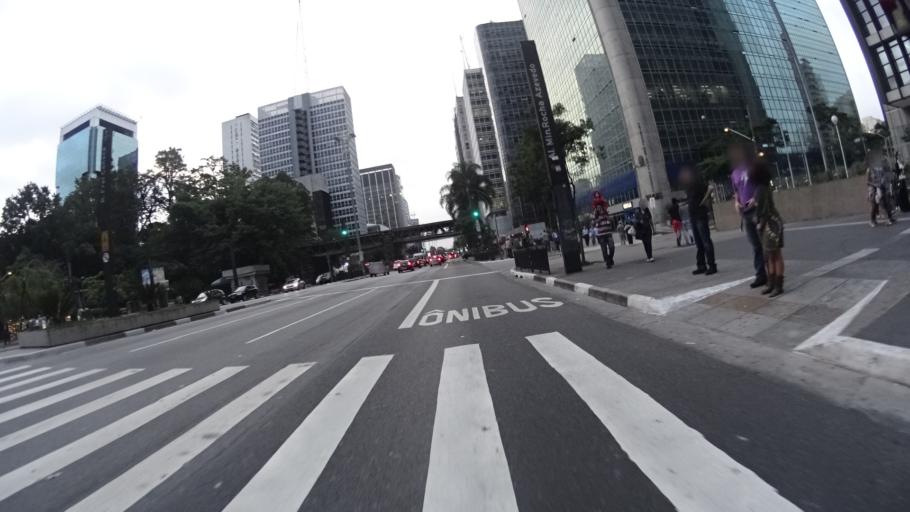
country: BR
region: Sao Paulo
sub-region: Sao Paulo
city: Sao Paulo
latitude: -23.5603
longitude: -46.6577
